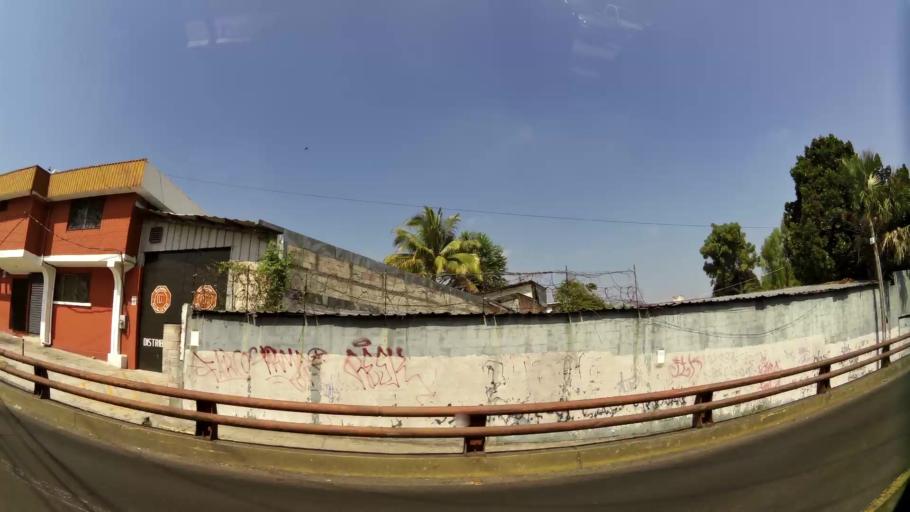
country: SV
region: San Salvador
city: San Salvador
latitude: 13.6969
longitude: -89.2170
